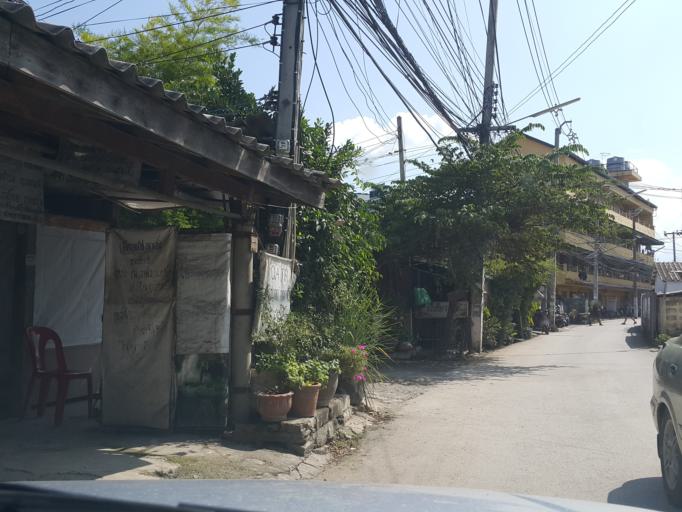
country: TH
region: Chiang Mai
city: Chiang Mai
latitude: 18.7916
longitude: 99.0270
